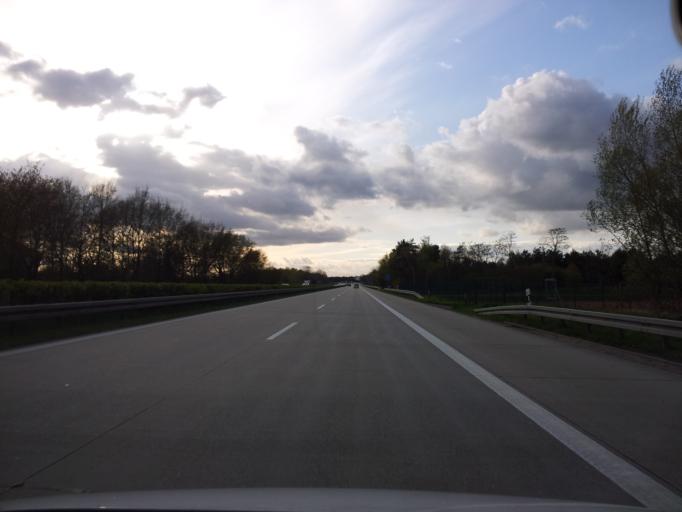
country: DE
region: Brandenburg
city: Cottbus
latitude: 51.7208
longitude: 14.3148
